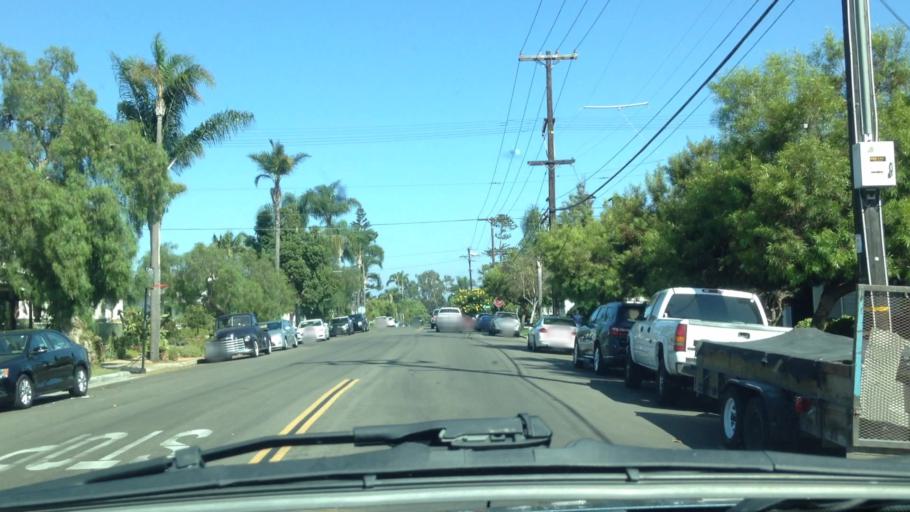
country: US
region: California
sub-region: San Diego County
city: Coronado
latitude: 32.6925
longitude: -117.1745
